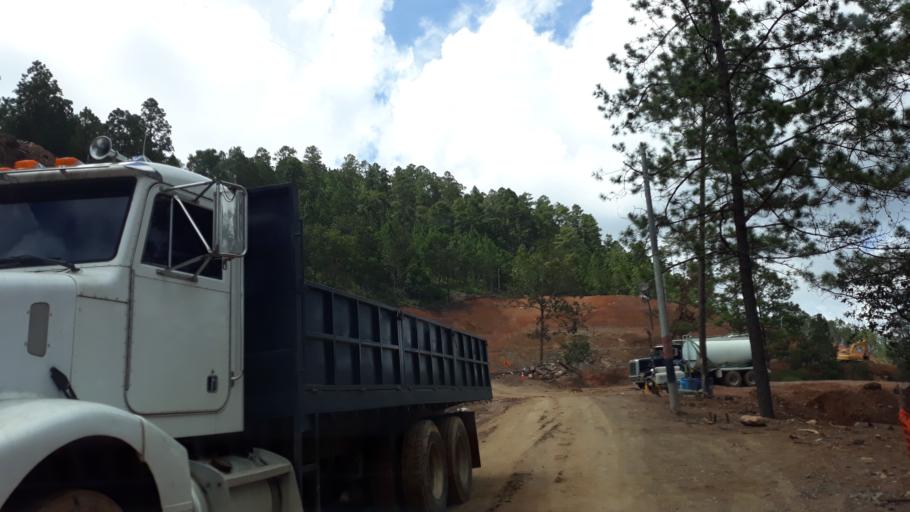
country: HN
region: El Paraiso
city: Santa Cruz
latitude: 13.7603
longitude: -86.6494
